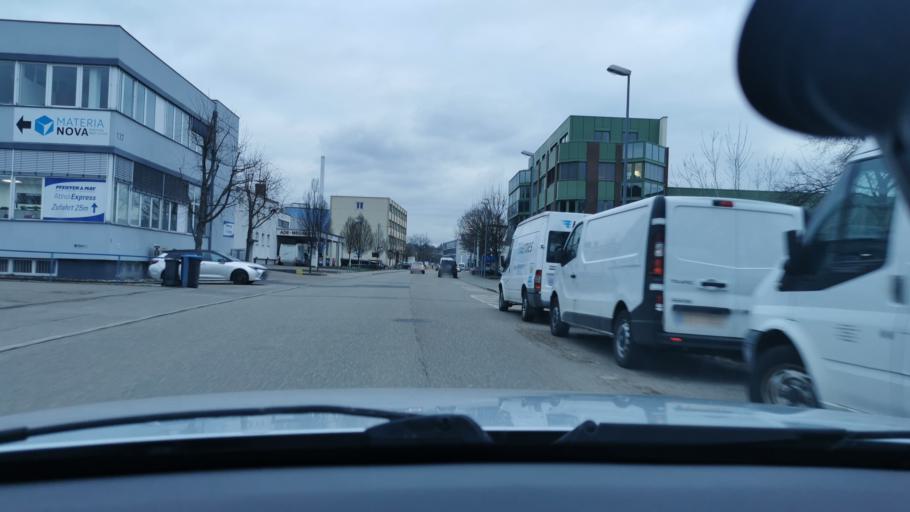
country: DE
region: Baden-Wuerttemberg
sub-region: Regierungsbezirk Stuttgart
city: Altbach
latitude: 48.7239
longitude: 9.3476
